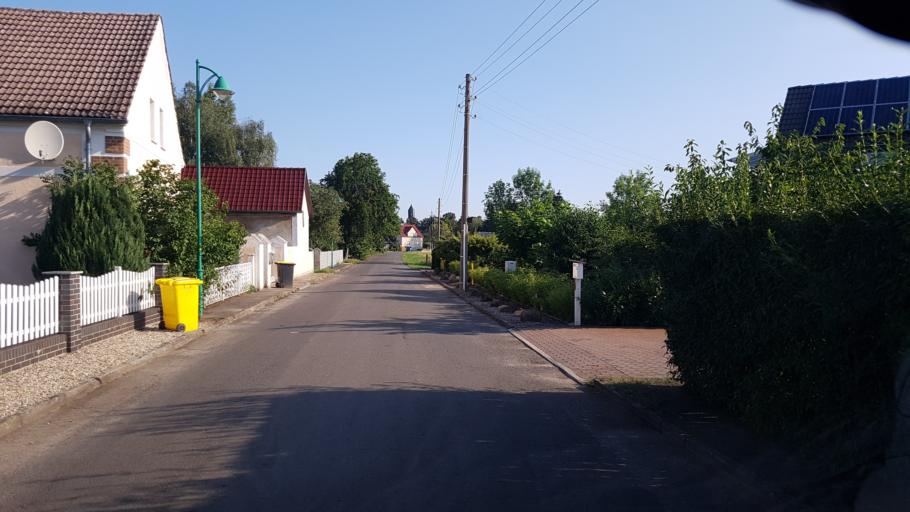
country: DE
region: Brandenburg
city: Luckau
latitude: 51.7992
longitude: 13.6478
